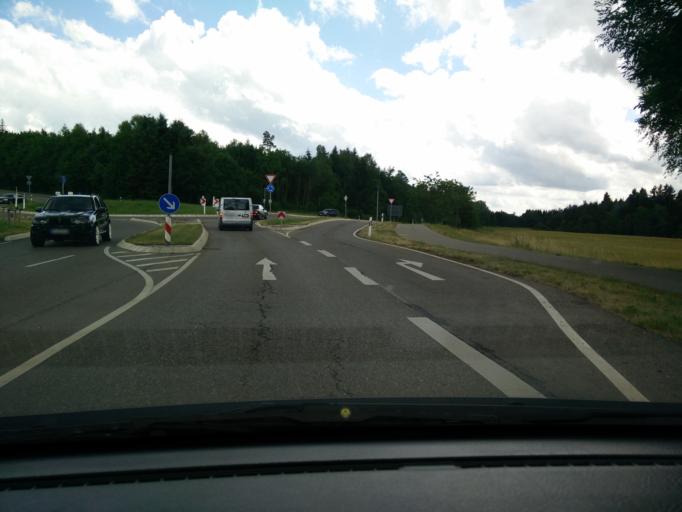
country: DE
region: Baden-Wuerttemberg
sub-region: Freiburg Region
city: Bad Durrheim
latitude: 48.0462
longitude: 8.5363
